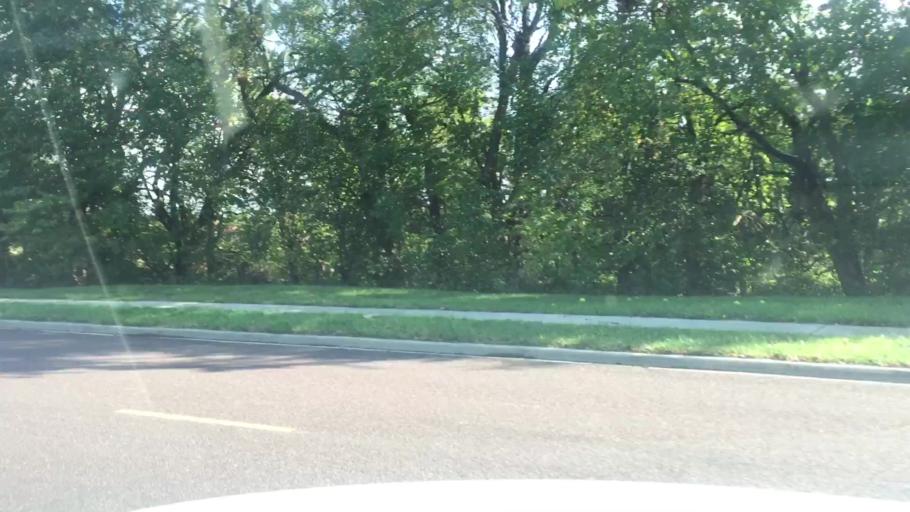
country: US
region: Kansas
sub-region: Johnson County
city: Lenexa
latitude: 38.8293
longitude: -94.6935
